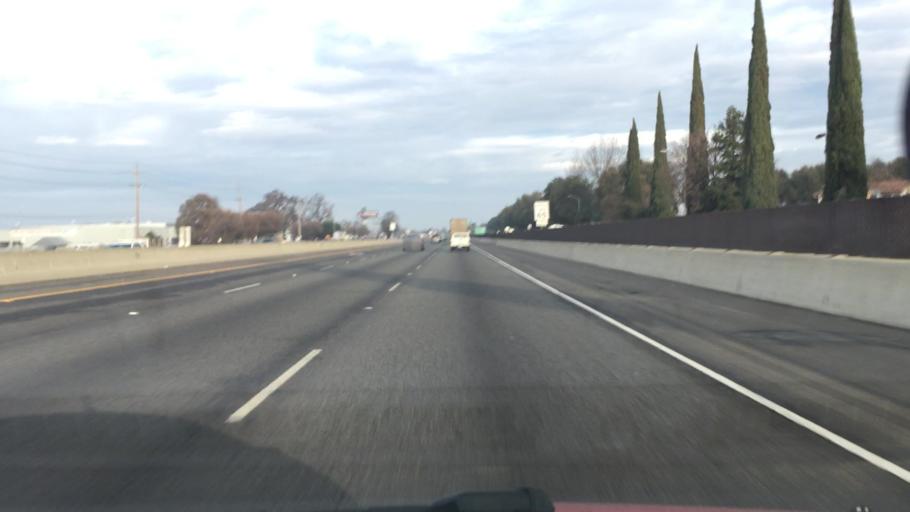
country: US
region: California
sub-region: Sacramento County
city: Elk Grove
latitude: 38.4003
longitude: -121.3828
